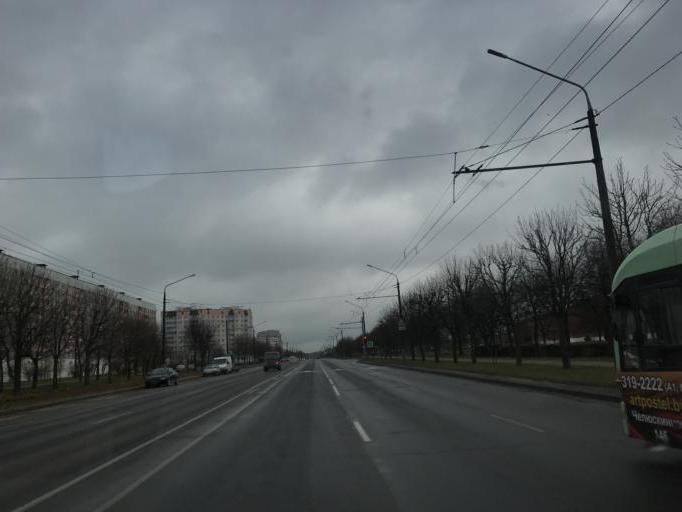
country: BY
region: Mogilev
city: Mahilyow
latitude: 53.8695
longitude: 30.3252
